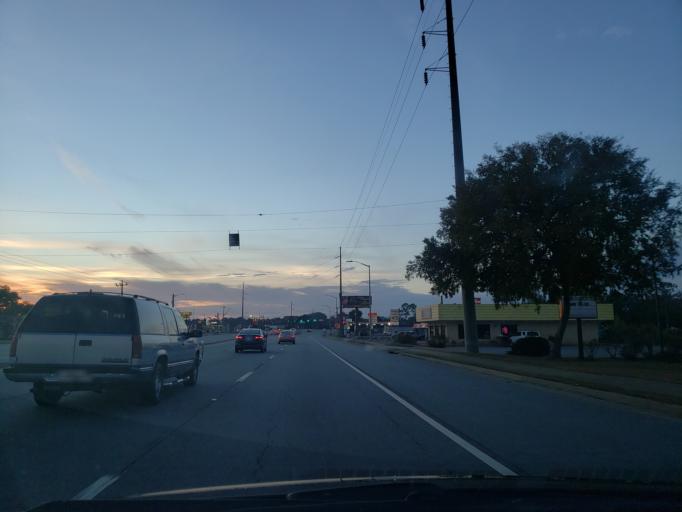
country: US
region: Georgia
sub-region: Dougherty County
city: Albany
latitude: 31.5710
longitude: -84.1051
